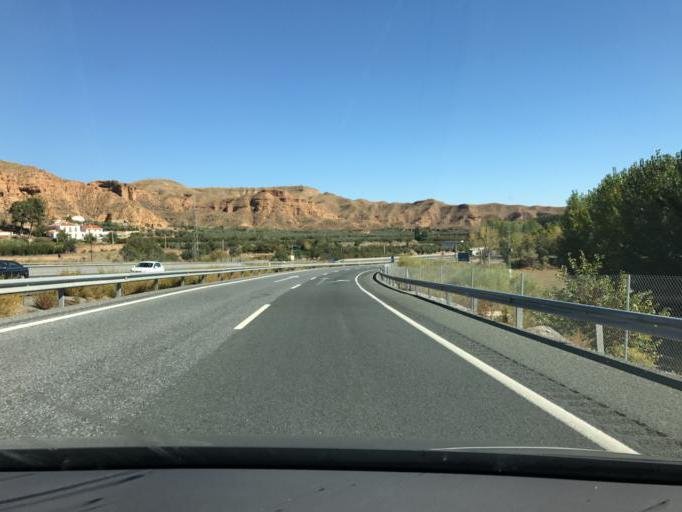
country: ES
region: Andalusia
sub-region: Provincia de Granada
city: Purullena
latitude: 37.3295
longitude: -3.2253
